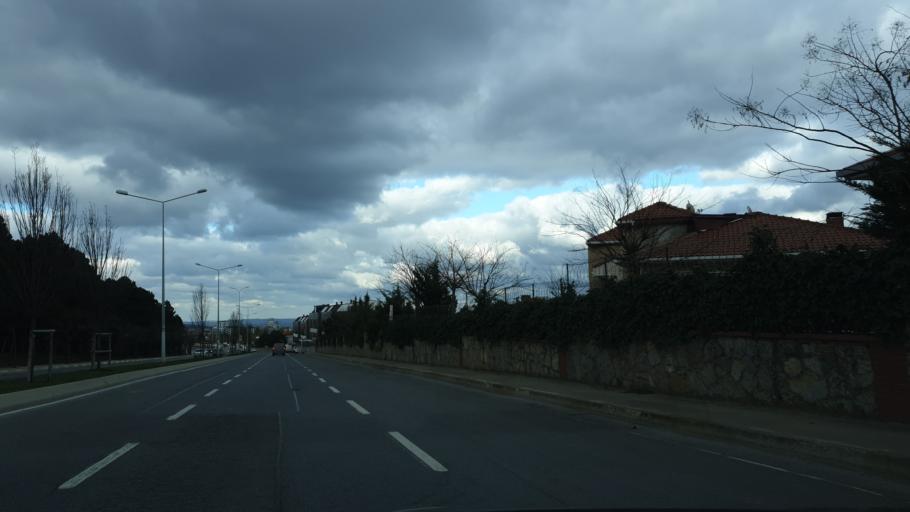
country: TR
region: Istanbul
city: Sultanbeyli
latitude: 40.9256
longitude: 29.2697
